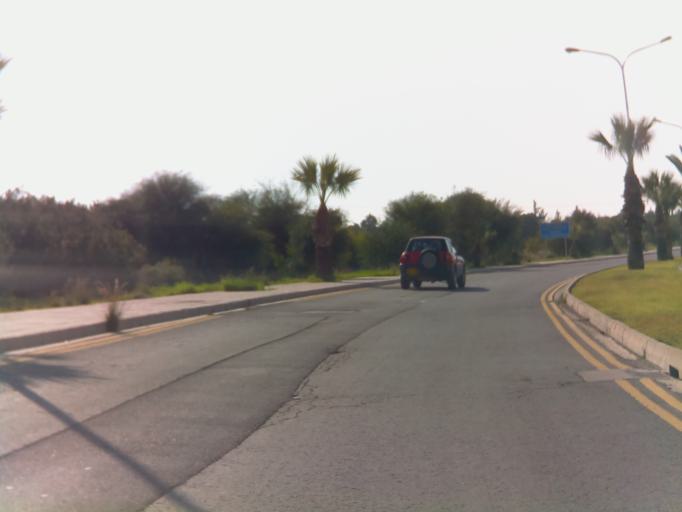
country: CY
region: Larnaka
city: Larnaca
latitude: 34.8931
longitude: 33.6325
